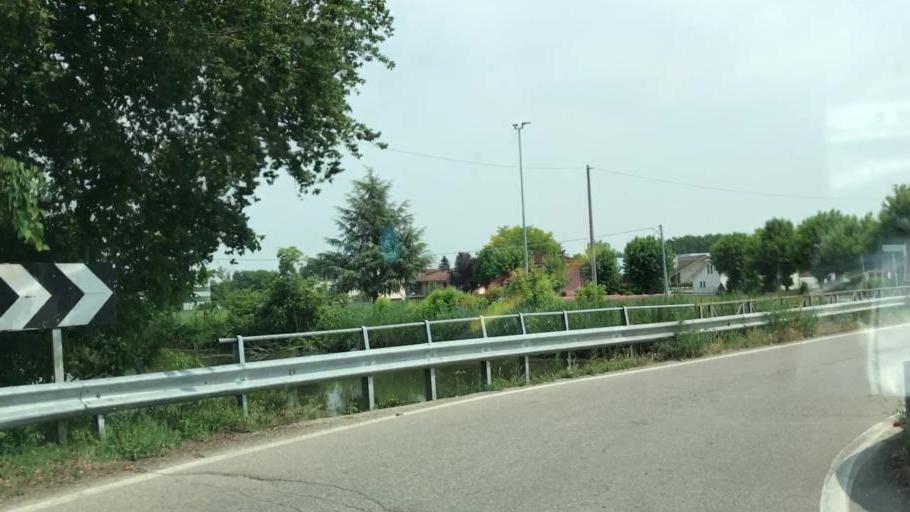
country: IT
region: Lombardy
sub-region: Provincia di Mantova
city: Dosolo
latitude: 45.0170
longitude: 10.6205
